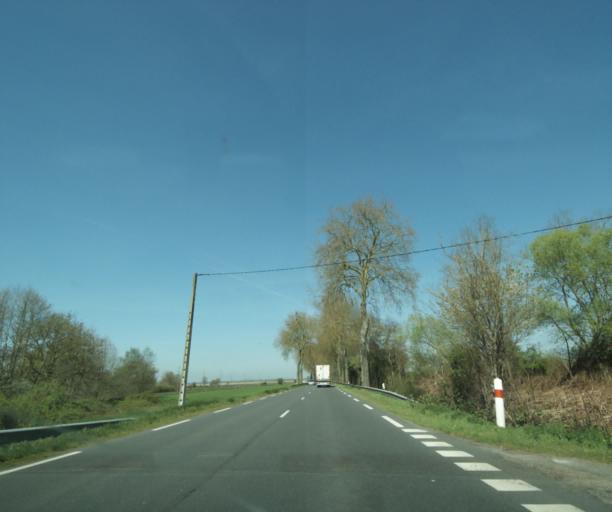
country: FR
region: Bourgogne
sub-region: Departement de la Nievre
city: Chantenay-Saint-Imbert
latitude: 46.6959
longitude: 3.2100
